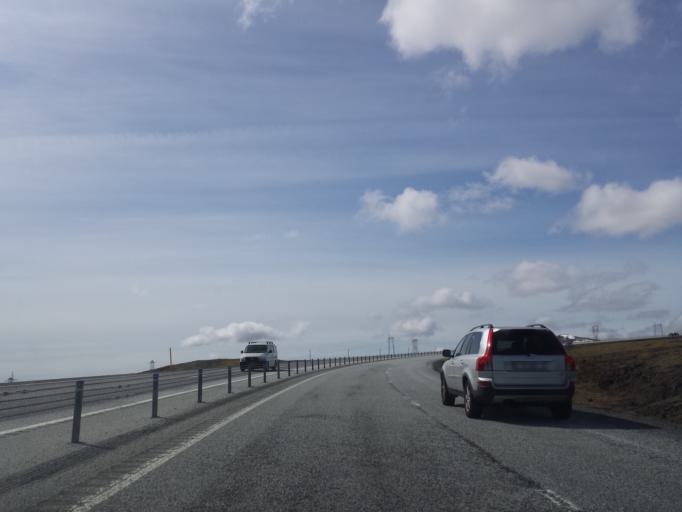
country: IS
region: South
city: Hveragerdi
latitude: 64.0115
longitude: -21.2360
